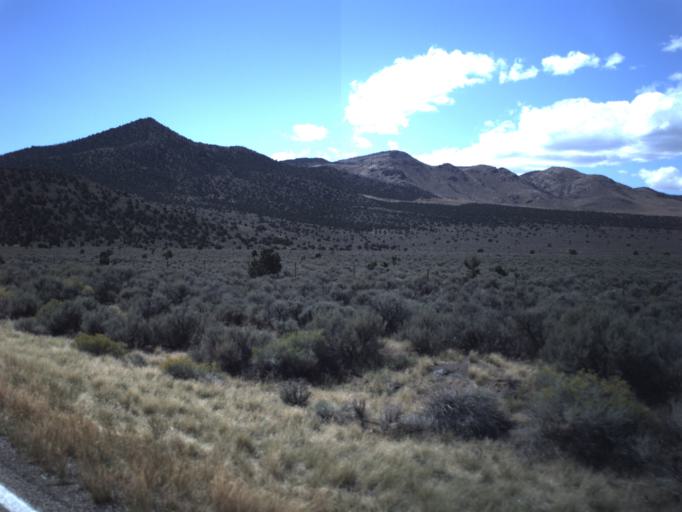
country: US
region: Utah
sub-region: Beaver County
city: Milford
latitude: 38.1375
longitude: -112.9601
